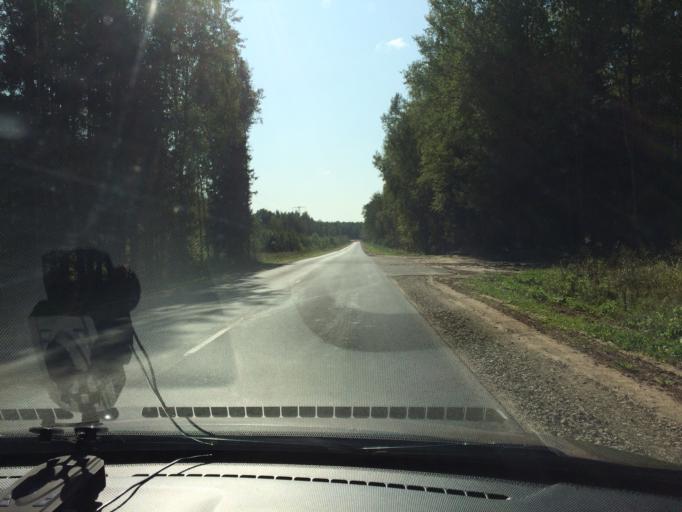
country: RU
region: Mariy-El
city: Surok
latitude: 56.5563
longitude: 48.3107
